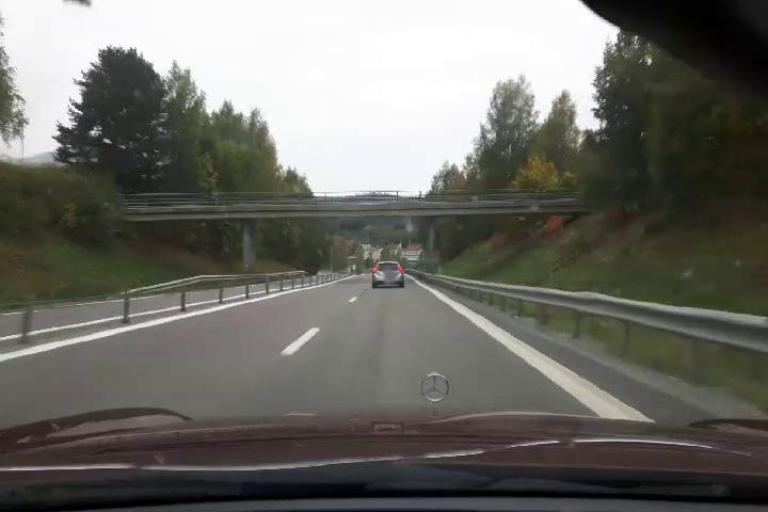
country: SE
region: Vaesternorrland
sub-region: Kramfors Kommun
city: Nordingra
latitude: 63.0531
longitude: 18.3275
